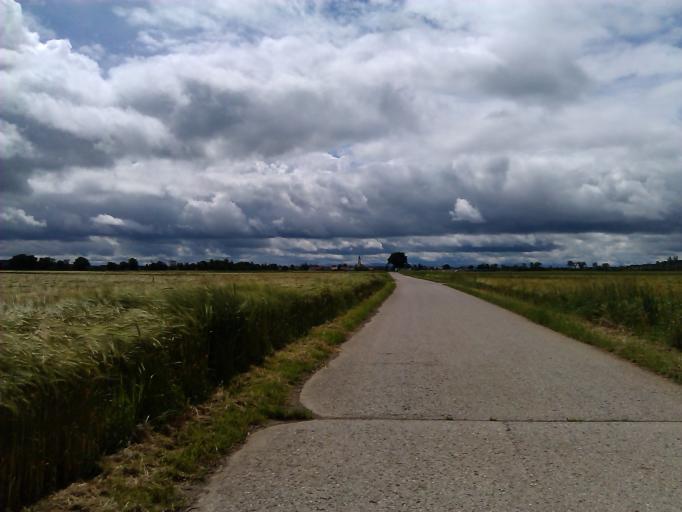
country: DE
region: Bavaria
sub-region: Swabia
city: Bad Worishofen
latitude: 47.9842
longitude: 10.6105
